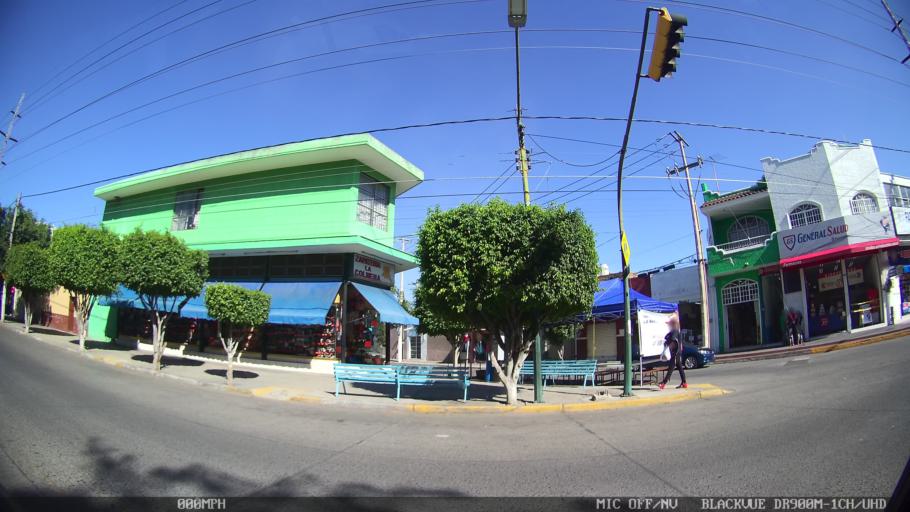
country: MX
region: Jalisco
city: Tlaquepaque
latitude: 20.6643
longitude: -103.2897
